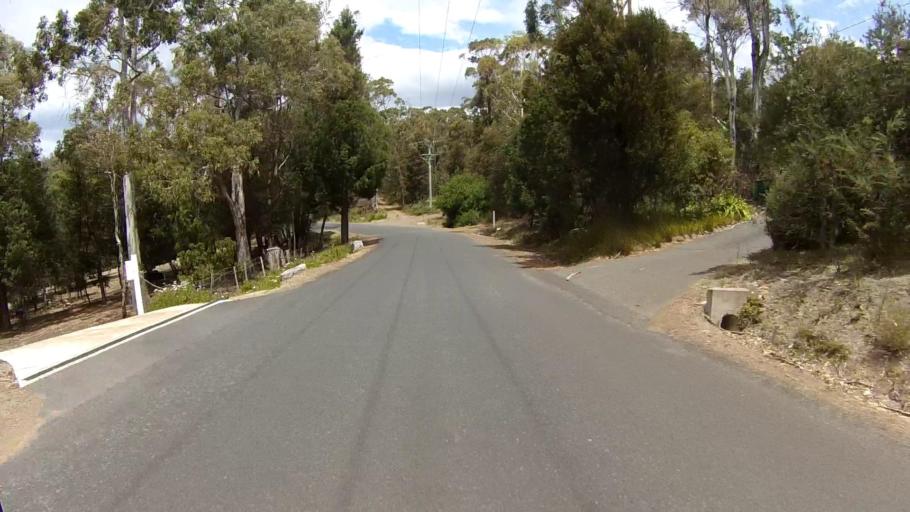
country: AU
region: Tasmania
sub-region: Sorell
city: Sorell
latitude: -42.5895
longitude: 147.9148
